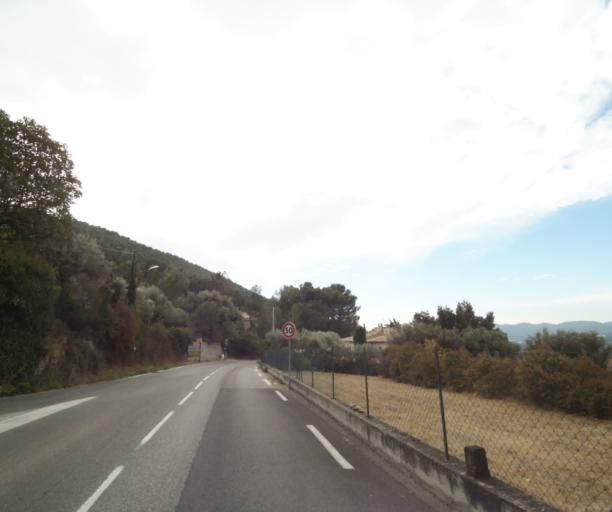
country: FR
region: Provence-Alpes-Cote d'Azur
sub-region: Departement des Bouches-du-Rhone
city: Ceyreste
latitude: 43.2233
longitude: 5.6491
